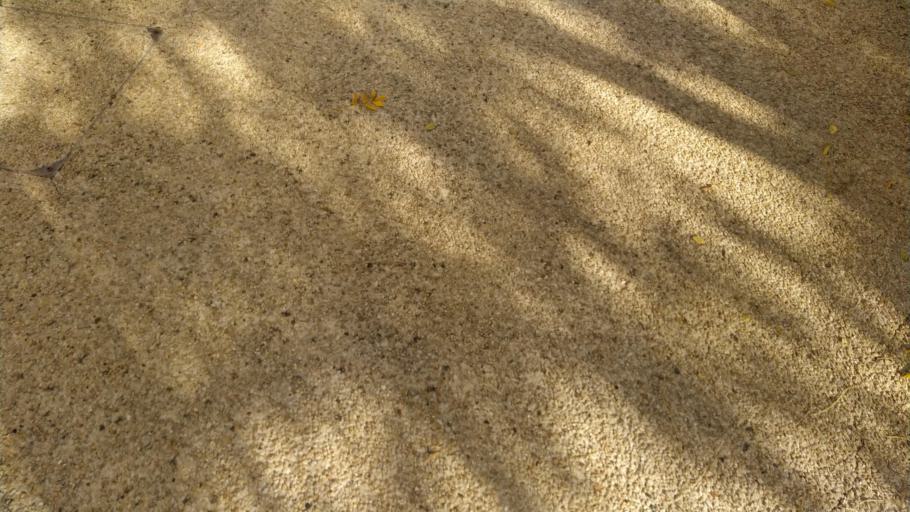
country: FR
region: Pays de la Loire
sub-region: Departement de la Loire-Atlantique
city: Chateaubriant
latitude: 47.7171
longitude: -1.3716
